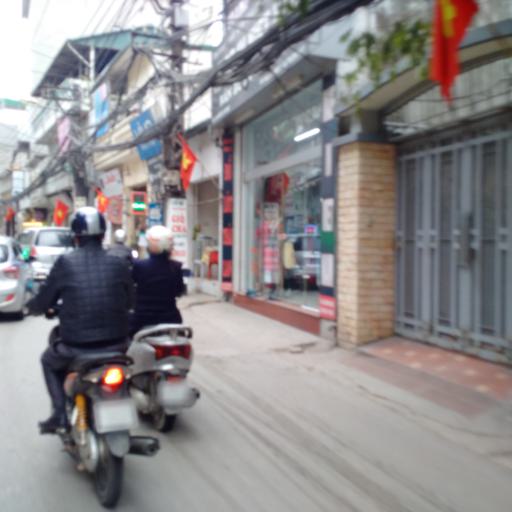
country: VN
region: Ha Noi
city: Cau Dien
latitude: 21.0593
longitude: 105.7827
